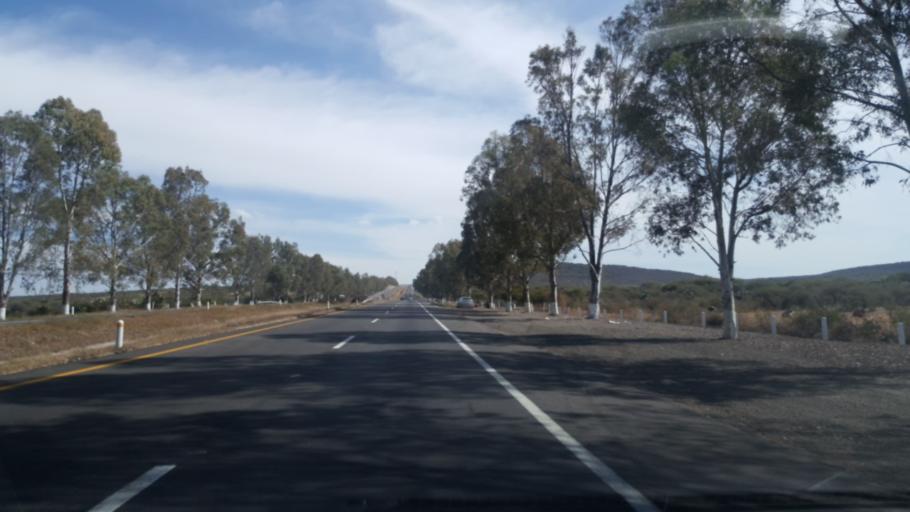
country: MX
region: Jalisco
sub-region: Lagos de Moreno
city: Cristeros [Fraccionamiento]
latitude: 21.2714
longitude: -101.9753
